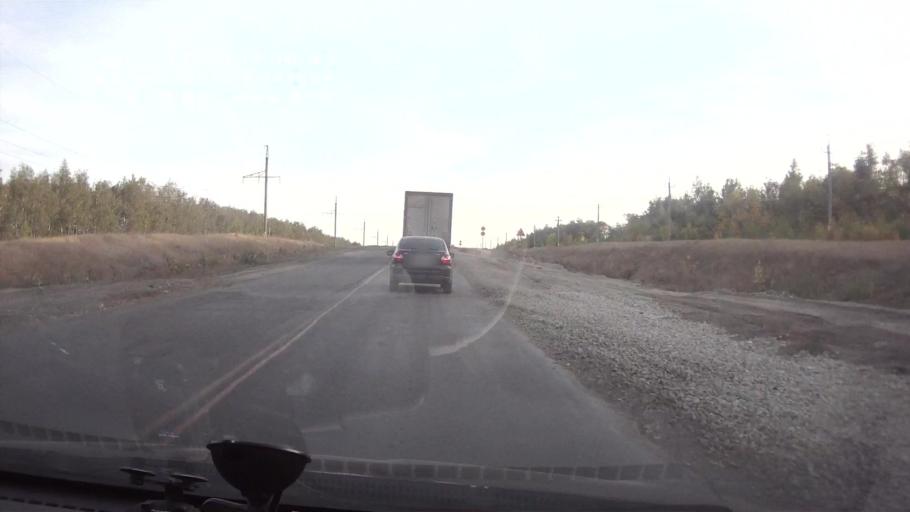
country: RU
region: Saratov
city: Krasnoarmeysk
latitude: 51.2027
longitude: 45.6477
